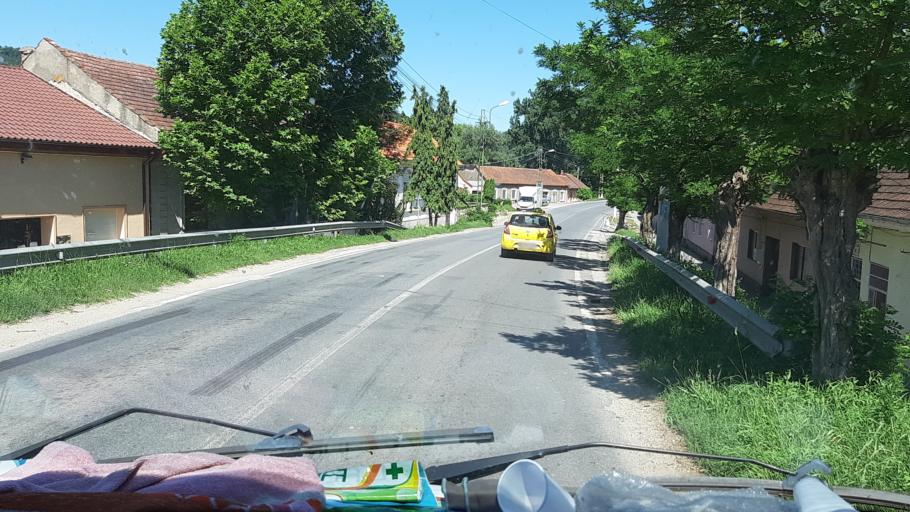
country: RO
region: Caras-Severin
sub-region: Oras Bocsa
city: Bocsa
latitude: 45.3816
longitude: 21.7843
